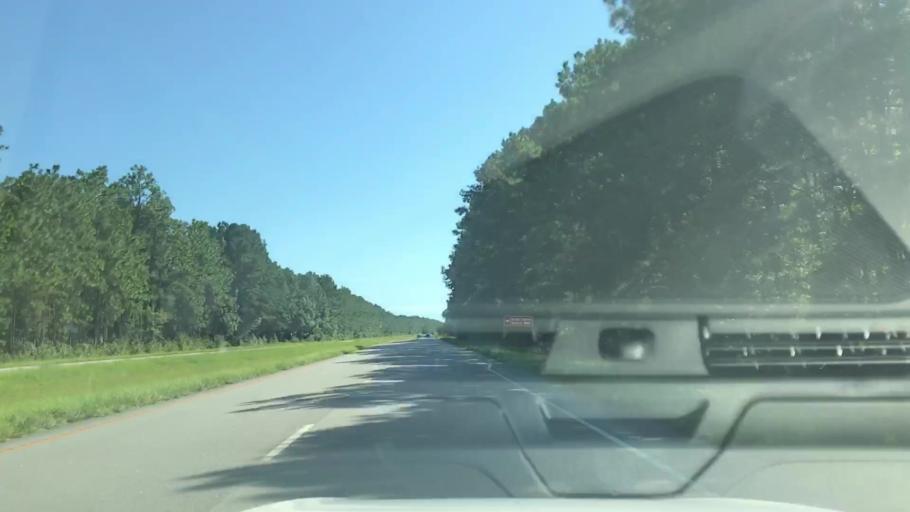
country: US
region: South Carolina
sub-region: Charleston County
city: Awendaw
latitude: 33.1313
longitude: -79.4461
